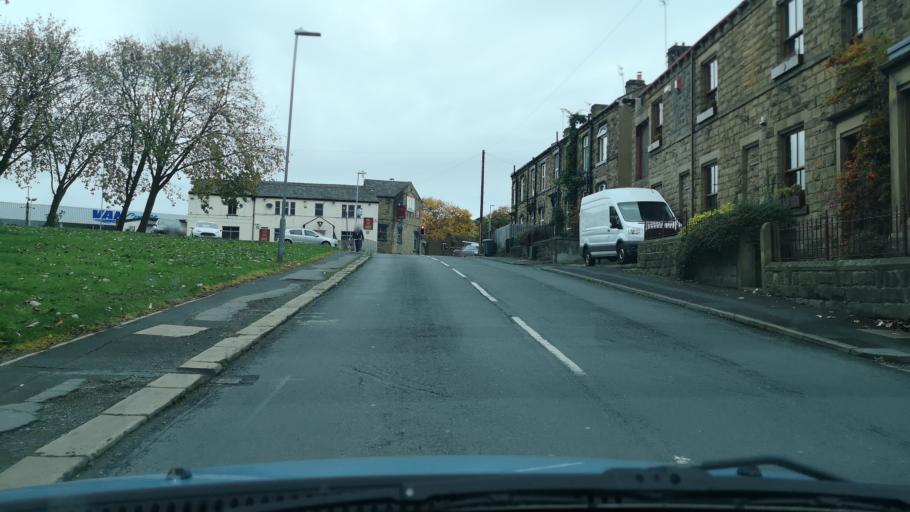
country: GB
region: England
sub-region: Kirklees
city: Heckmondwike
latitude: 53.7282
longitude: -1.6609
